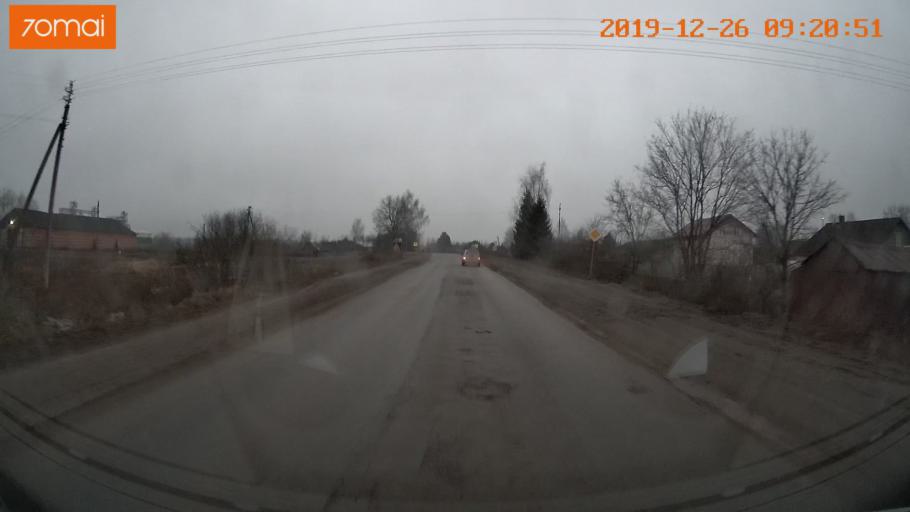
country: RU
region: Vologda
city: Gryazovets
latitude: 58.9649
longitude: 40.2275
